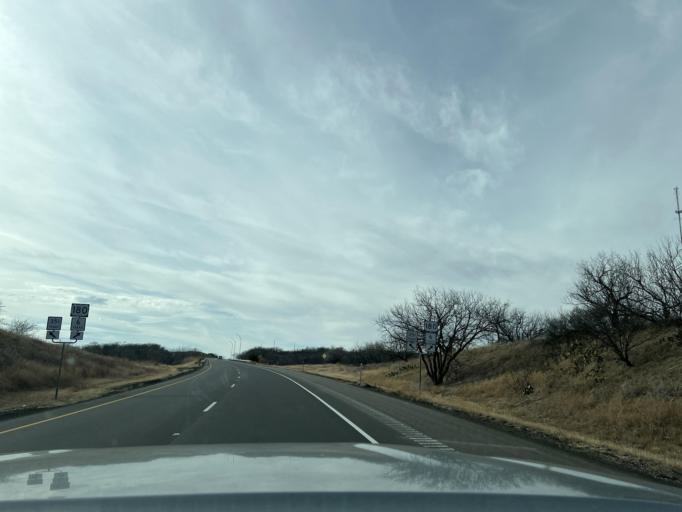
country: US
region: Texas
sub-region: Shackelford County
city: Albany
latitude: 32.7077
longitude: -99.4185
